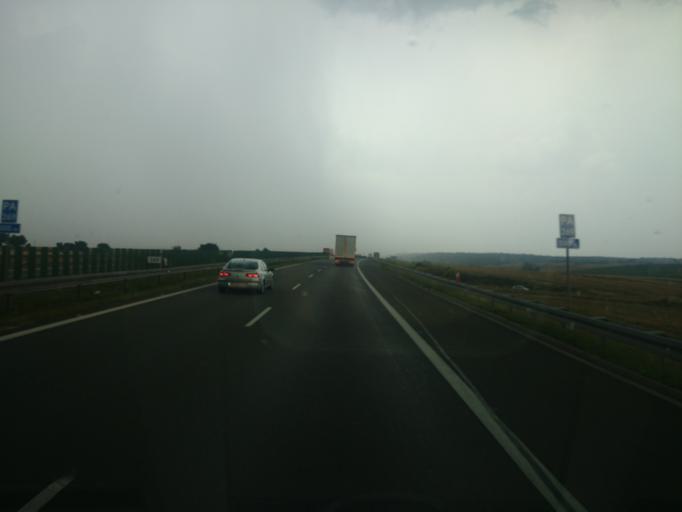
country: PL
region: Opole Voivodeship
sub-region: Powiat strzelecki
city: Lesnica
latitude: 50.4652
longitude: 18.2169
